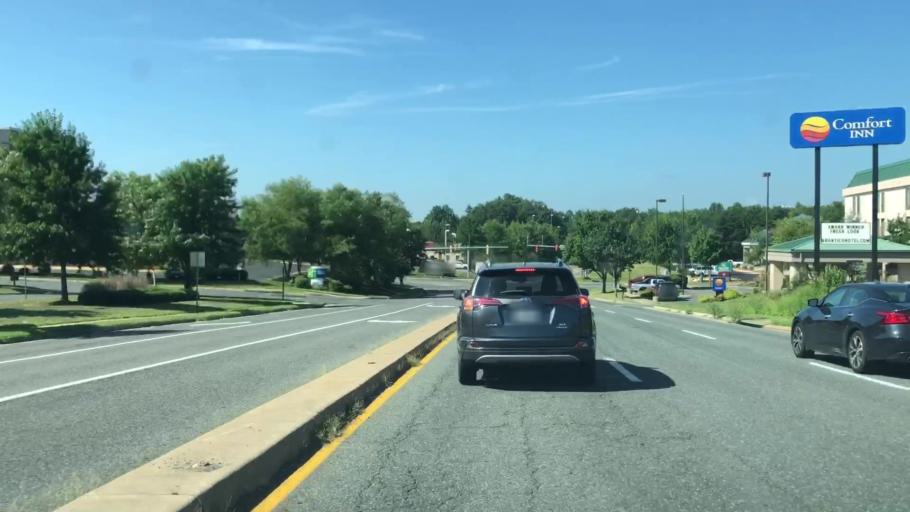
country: US
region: Virginia
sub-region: Stafford County
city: Aquia Harbour
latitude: 38.4683
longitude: -77.4126
